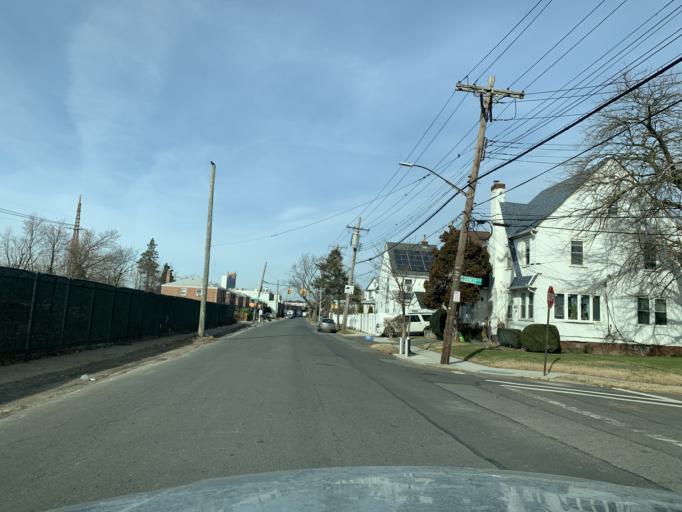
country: US
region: New York
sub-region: Queens County
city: Jamaica
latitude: 40.6961
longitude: -73.7686
